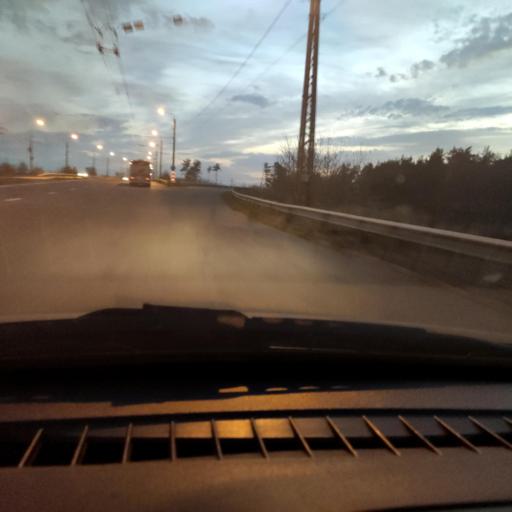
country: RU
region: Samara
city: Zhigulevsk
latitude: 53.5209
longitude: 49.5397
